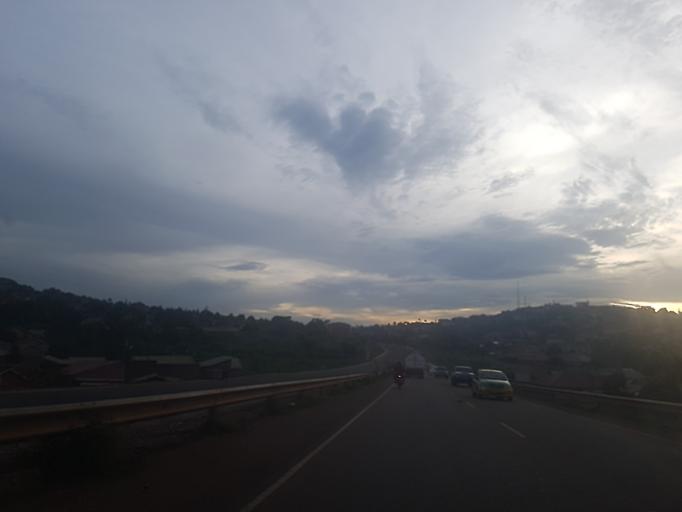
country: UG
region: Central Region
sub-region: Wakiso District
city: Kireka
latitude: 0.3693
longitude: 32.6204
